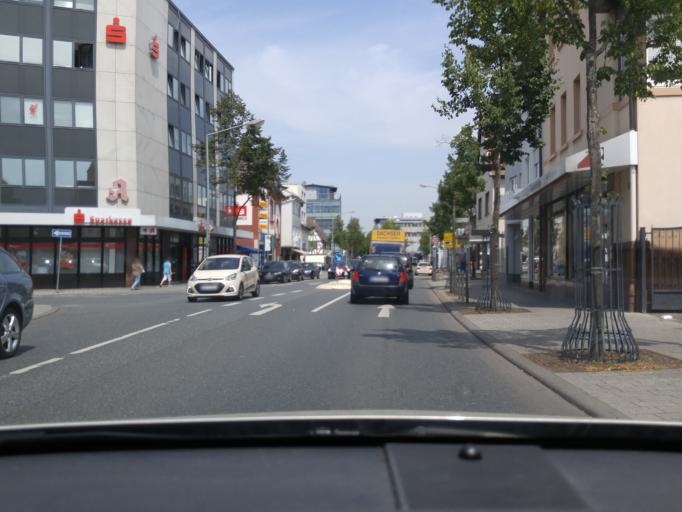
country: DE
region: Hesse
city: Dreieich
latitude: 50.0174
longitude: 8.6953
